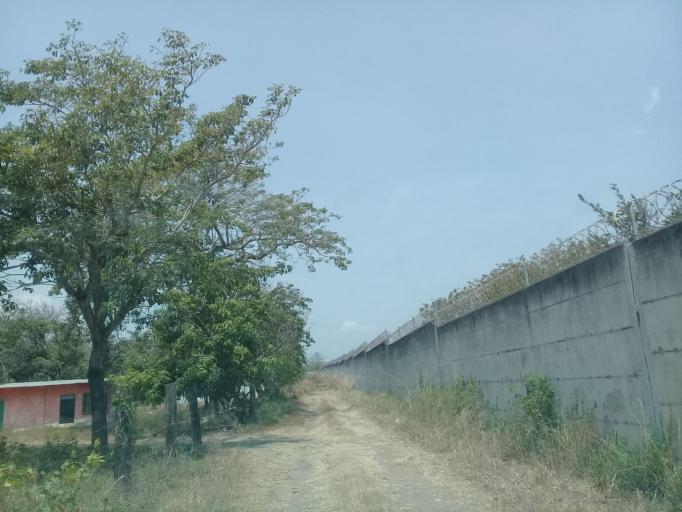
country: MX
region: Veracruz
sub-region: Veracruz
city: Hacienda Sotavento
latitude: 19.1350
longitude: -96.1825
